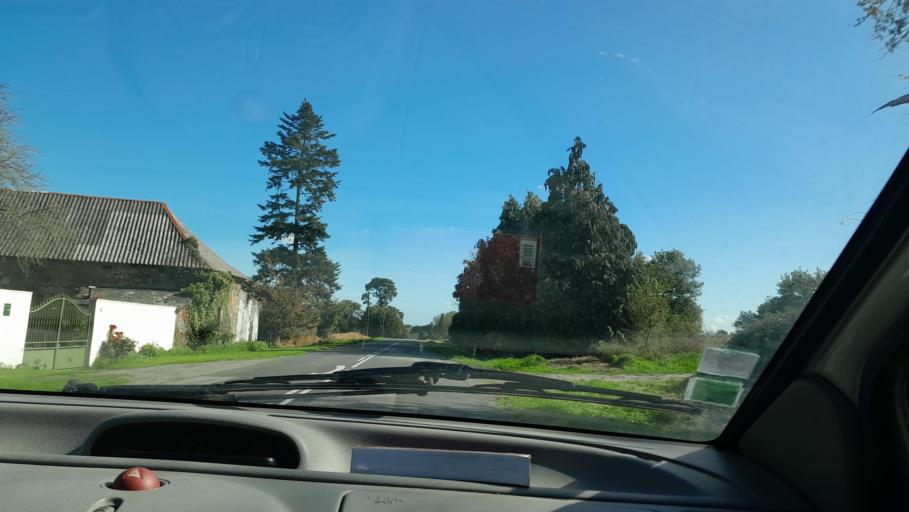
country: FR
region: Pays de la Loire
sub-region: Departement de la Mayenne
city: Cosse-le-Vivien
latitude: 47.9551
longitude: -0.9480
